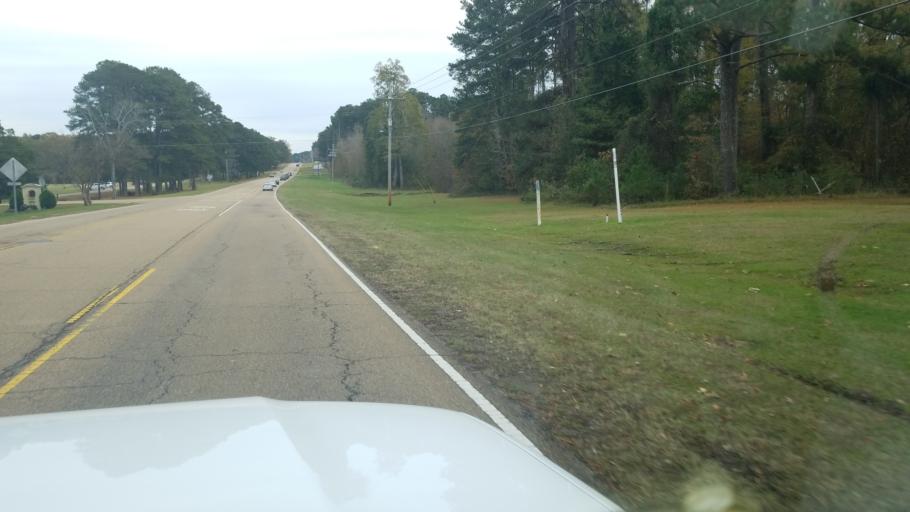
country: US
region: Mississippi
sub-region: Madison County
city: Ridgeland
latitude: 32.3781
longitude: -90.0305
